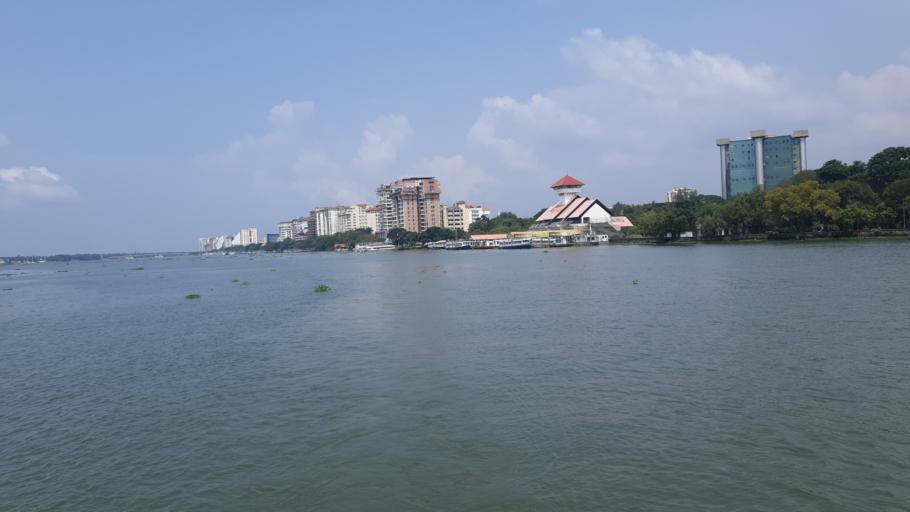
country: IN
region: Kerala
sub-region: Ernakulam
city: Cochin
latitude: 9.9702
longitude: 76.2782
